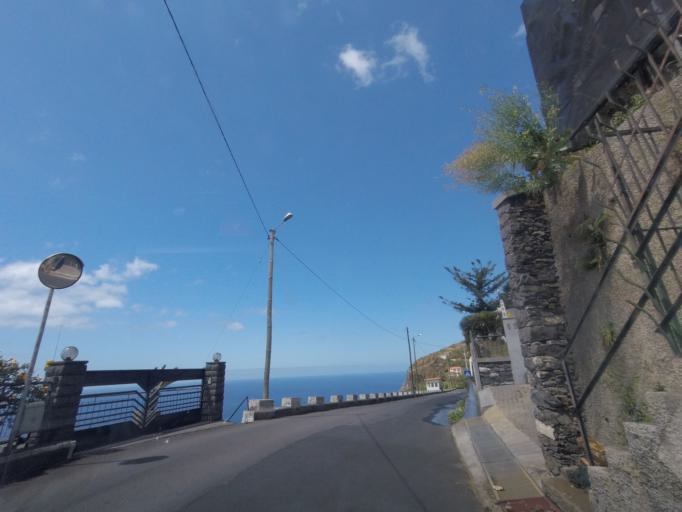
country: PT
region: Madeira
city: Ponta do Sol
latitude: 32.6848
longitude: -17.0874
